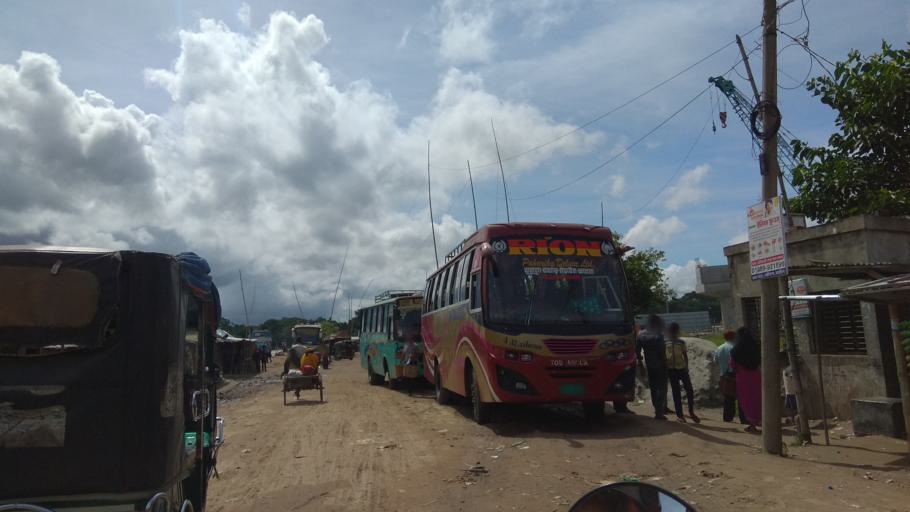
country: BD
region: Khulna
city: Kalia
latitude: 23.1948
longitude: 89.6881
